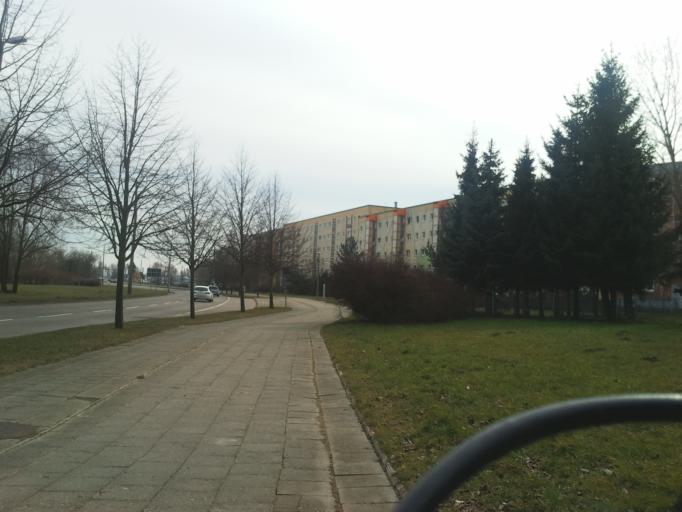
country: DE
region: Mecklenburg-Vorpommern
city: Dierkow-Neu
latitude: 54.1051
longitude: 12.1769
